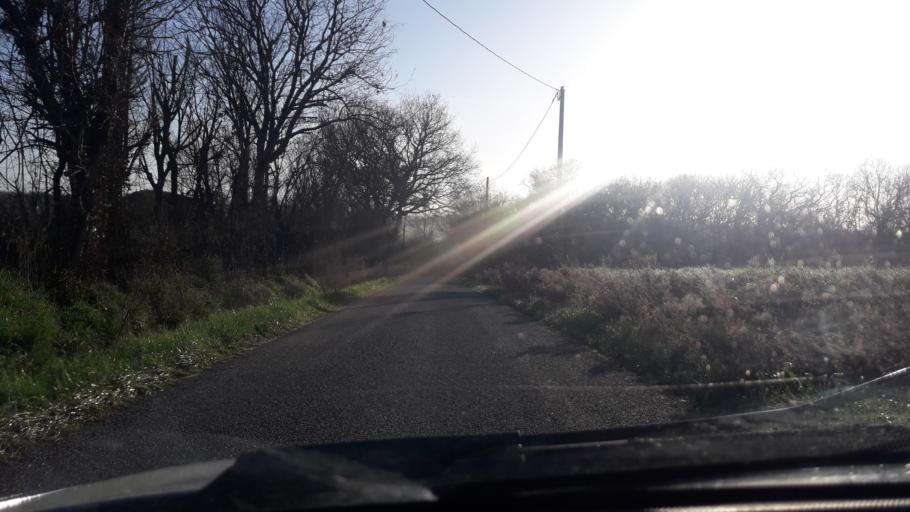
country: FR
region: Midi-Pyrenees
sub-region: Departement du Gers
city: Gimont
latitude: 43.6582
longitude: 0.9701
